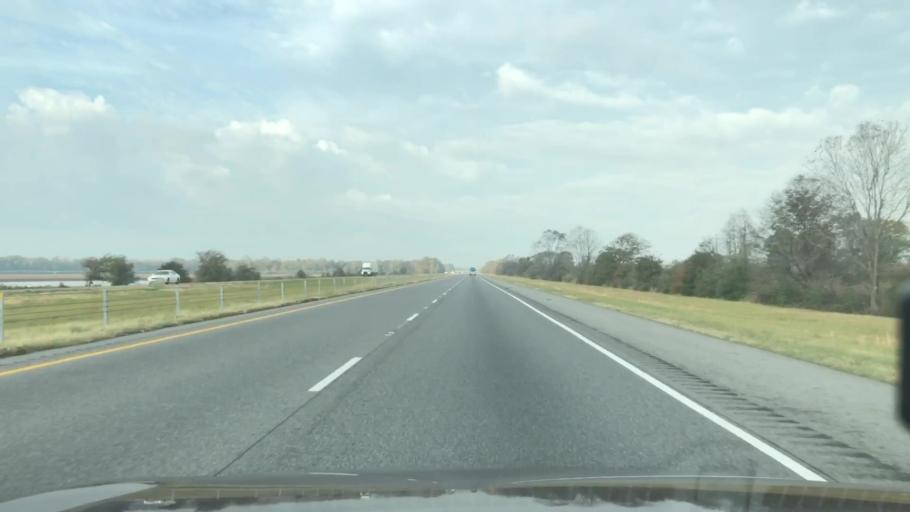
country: US
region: Louisiana
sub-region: Richland Parish
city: Delhi
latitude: 32.4227
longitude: -91.3422
